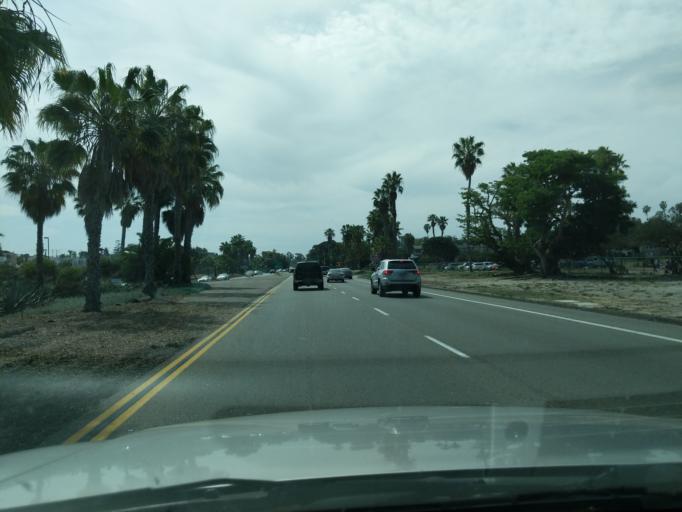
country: US
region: California
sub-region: San Diego County
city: Coronado
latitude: 32.7535
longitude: -117.2372
